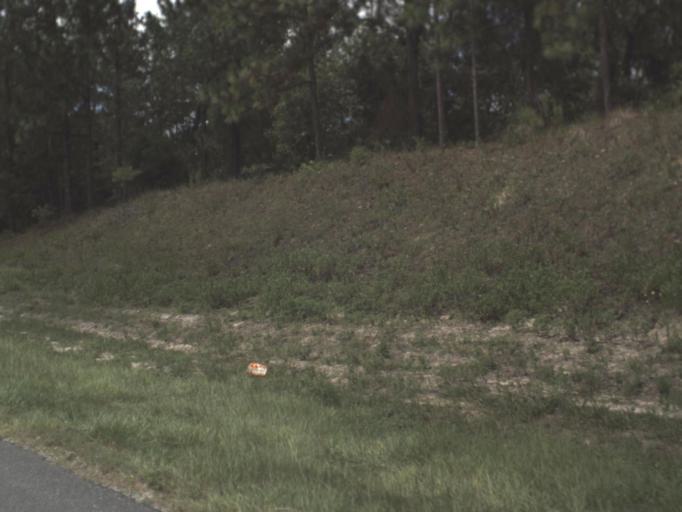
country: US
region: Florida
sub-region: Gilchrist County
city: Trenton
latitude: 29.7804
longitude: -82.8667
